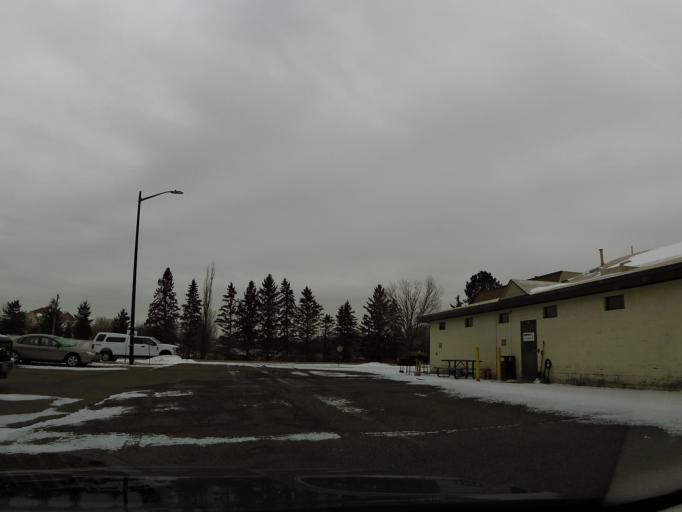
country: US
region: Minnesota
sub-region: Hennepin County
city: Medina
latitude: 45.0420
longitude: -93.5620
